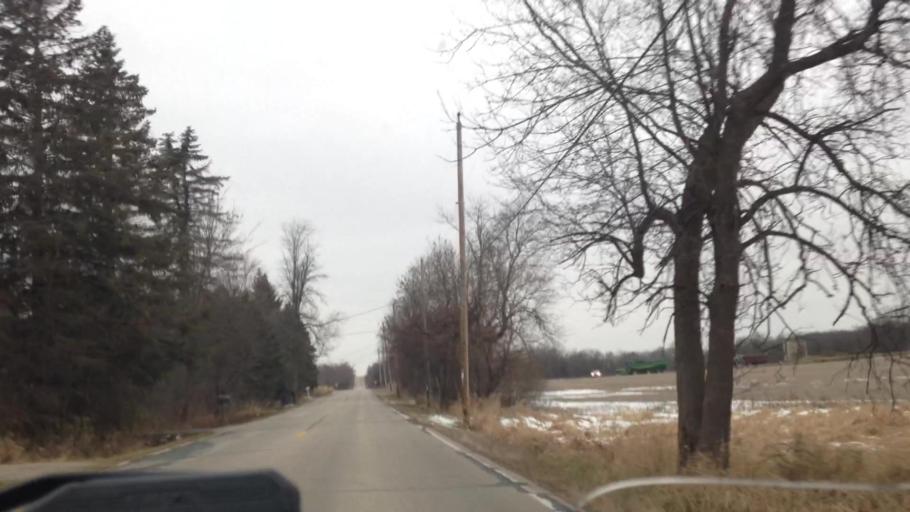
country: US
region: Wisconsin
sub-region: Waukesha County
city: Lannon
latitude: 43.1701
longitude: -88.1510
